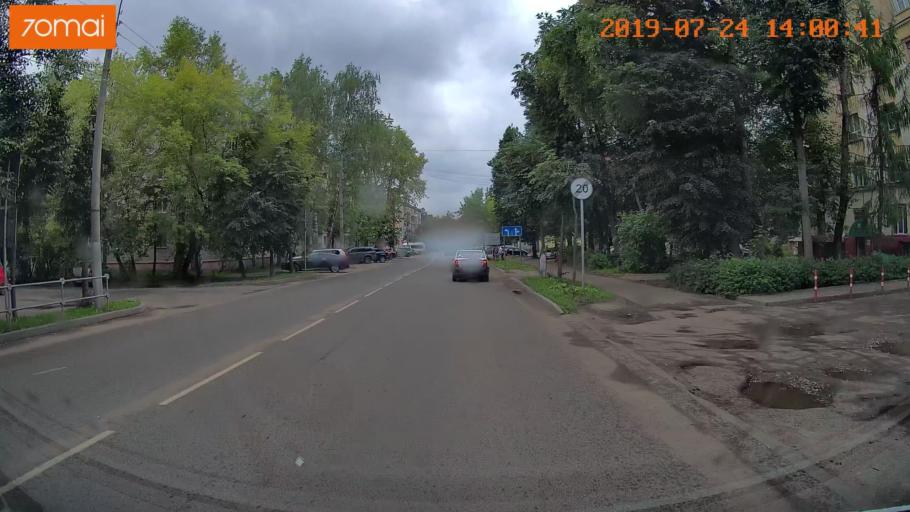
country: RU
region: Ivanovo
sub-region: Gorod Ivanovo
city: Ivanovo
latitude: 57.0123
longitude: 40.9789
